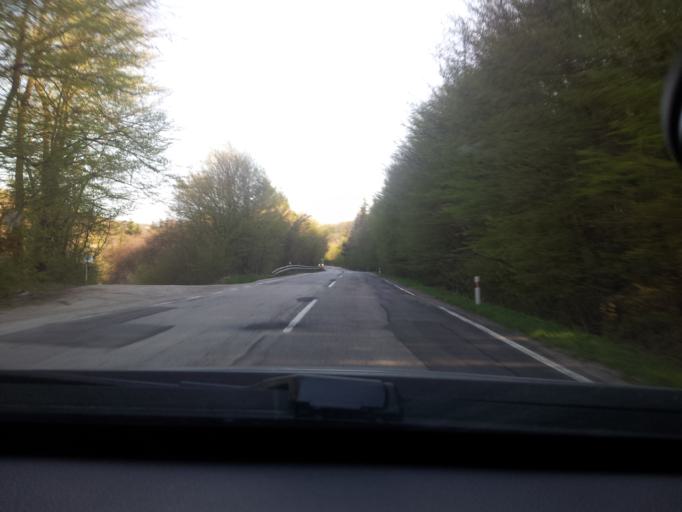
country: SK
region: Nitriansky
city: Zlate Moravce
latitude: 48.4822
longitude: 18.4176
